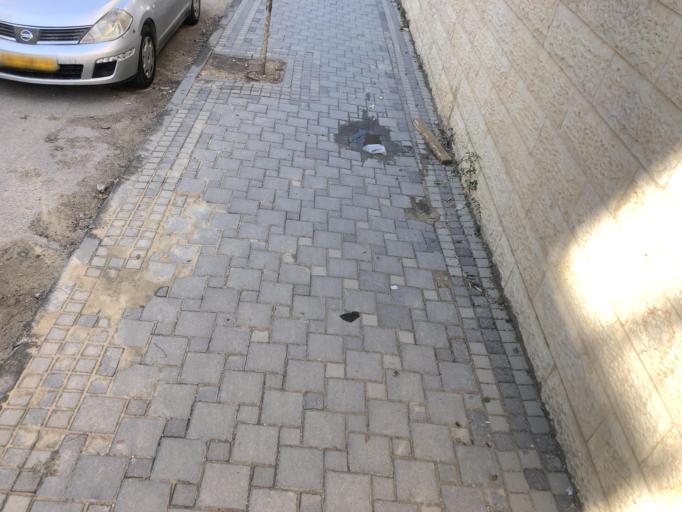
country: IL
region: Jerusalem
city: Modiin Ilit
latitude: 31.9222
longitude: 35.0511
